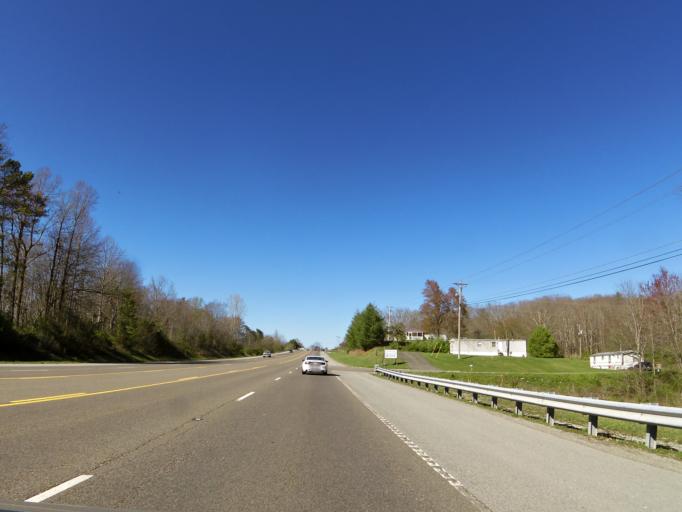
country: US
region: Tennessee
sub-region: Scott County
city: Oneida
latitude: 36.4653
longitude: -84.5472
